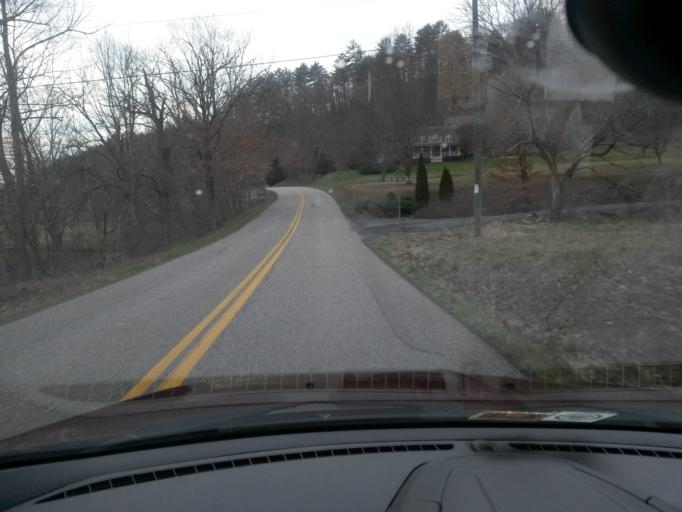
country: US
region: Virginia
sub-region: Bath County
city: Warm Springs
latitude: 37.9997
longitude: -79.8837
